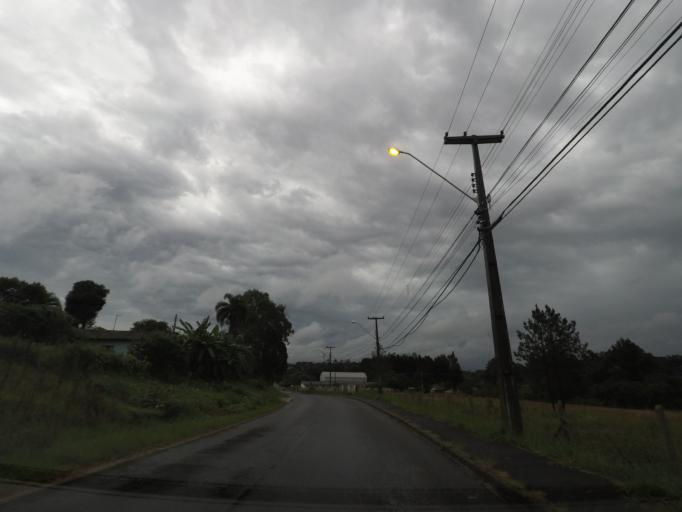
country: BR
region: Parana
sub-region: Campo Largo
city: Campo Largo
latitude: -25.4454
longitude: -49.4590
